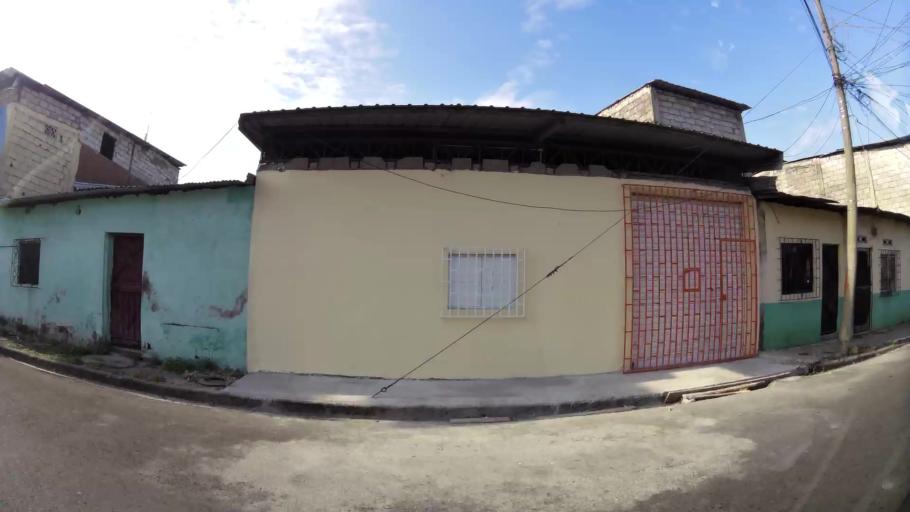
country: EC
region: Guayas
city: Guayaquil
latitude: -2.2103
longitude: -79.9021
